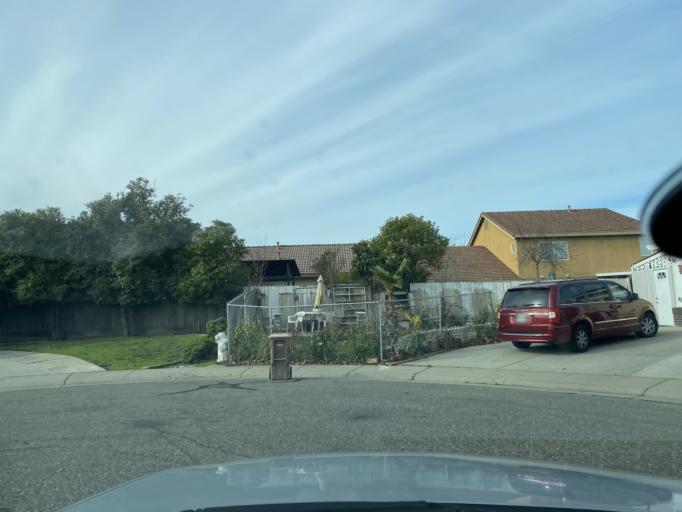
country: US
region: California
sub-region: Sacramento County
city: Elk Grove
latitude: 38.4425
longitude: -121.3876
